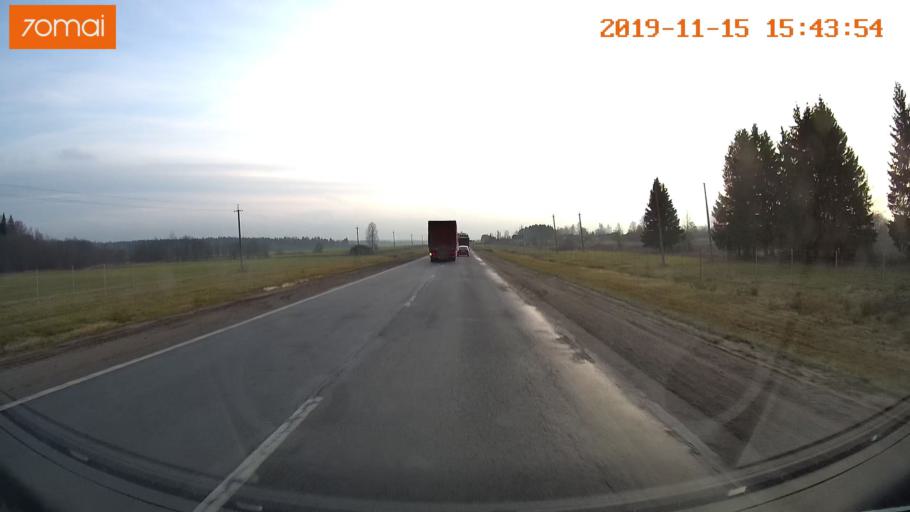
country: RU
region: Jaroslavl
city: Danilov
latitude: 57.9766
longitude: 40.0248
